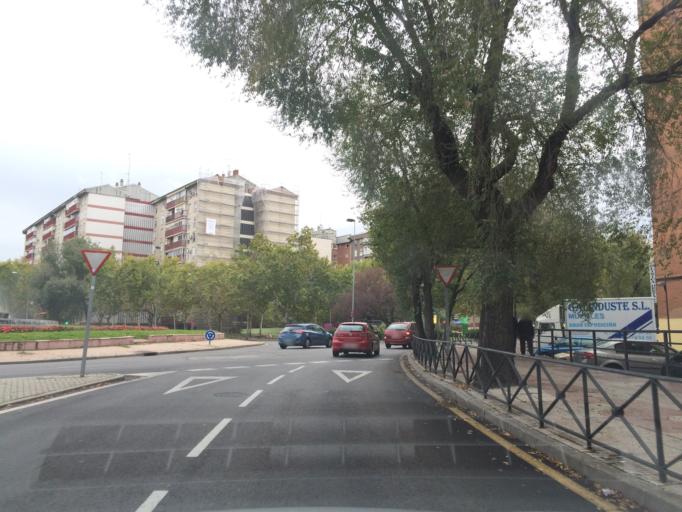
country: ES
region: Madrid
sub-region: Provincia de Madrid
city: Alcorcon
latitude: 40.3479
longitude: -3.8185
